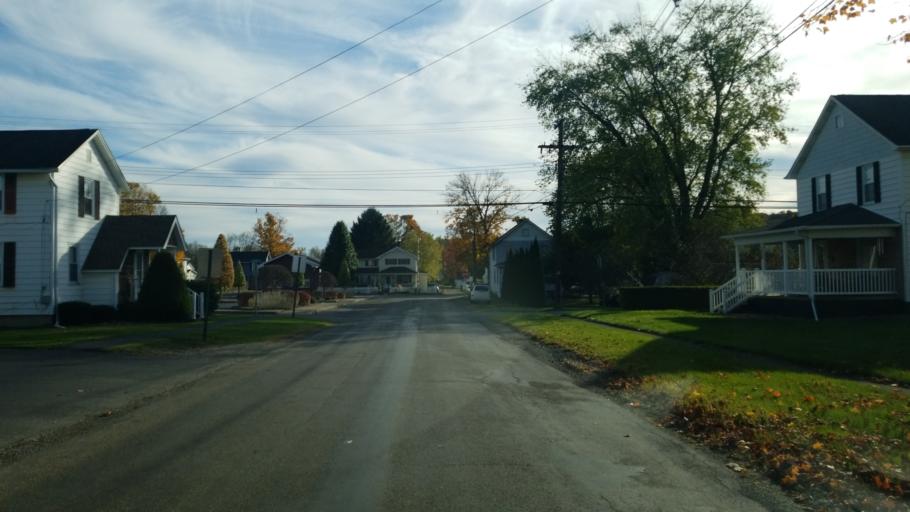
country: US
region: Pennsylvania
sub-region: Jefferson County
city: Brockway
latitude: 41.2472
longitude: -78.7840
